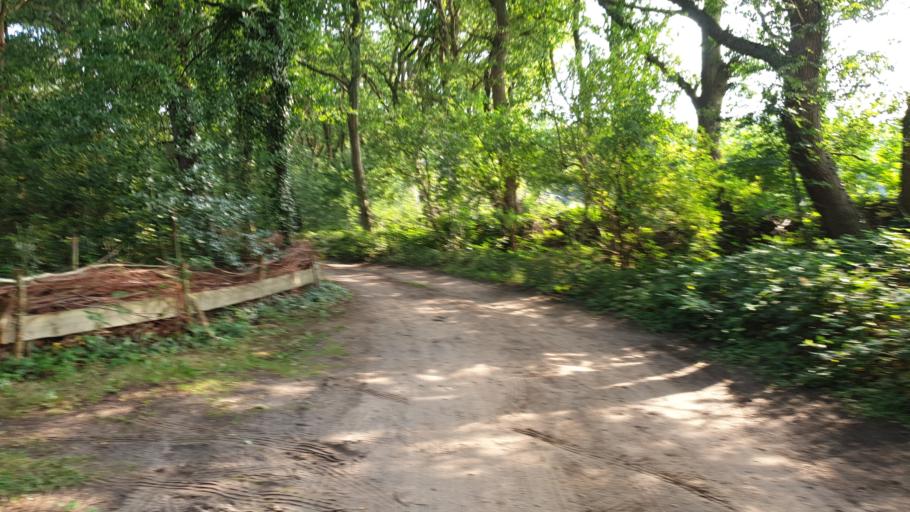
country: NL
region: Drenthe
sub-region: Gemeente Tynaarlo
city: Tynaarlo
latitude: 53.0679
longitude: 6.6537
